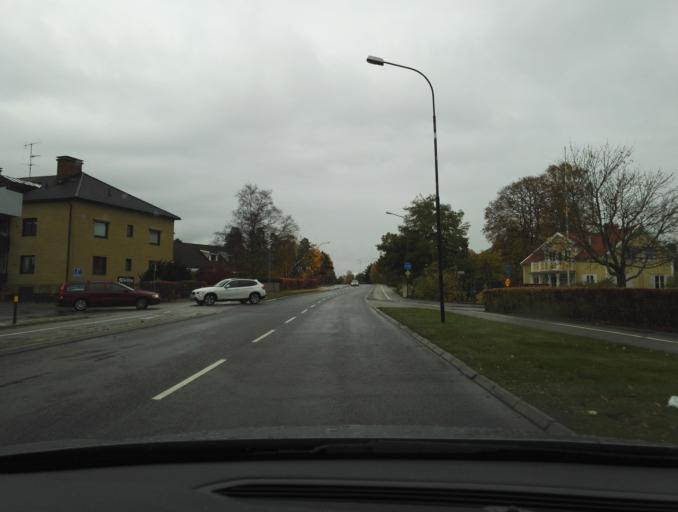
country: SE
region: Kronoberg
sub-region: Vaxjo Kommun
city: Vaexjoe
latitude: 56.8850
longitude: 14.7525
